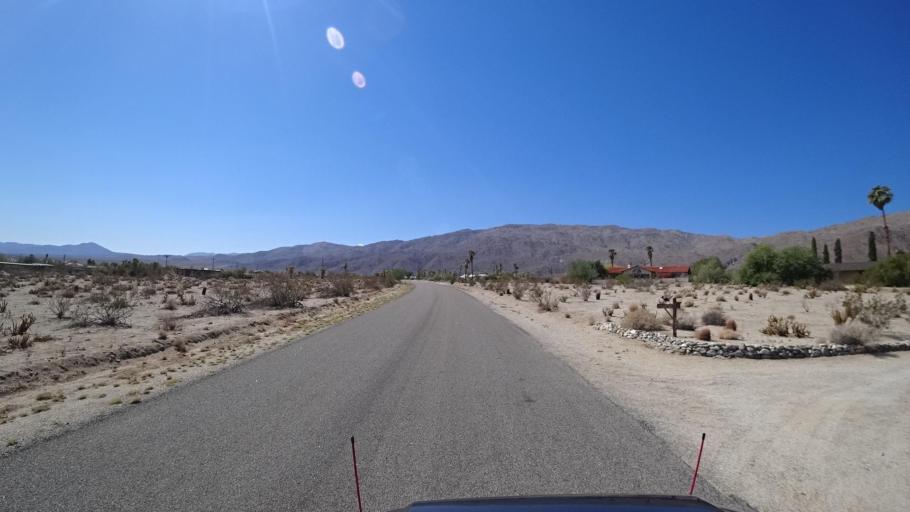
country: US
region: California
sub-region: San Diego County
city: Borrego Springs
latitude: 33.2281
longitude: -116.3921
